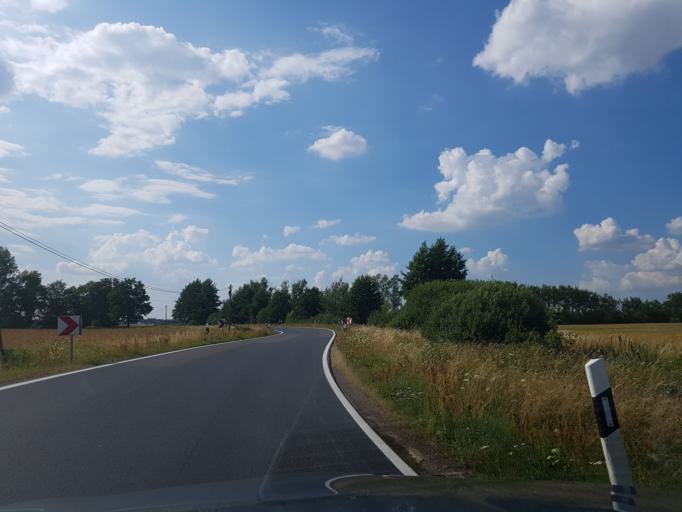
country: DE
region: Brandenburg
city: Herzberg
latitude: 51.6867
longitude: 13.2862
